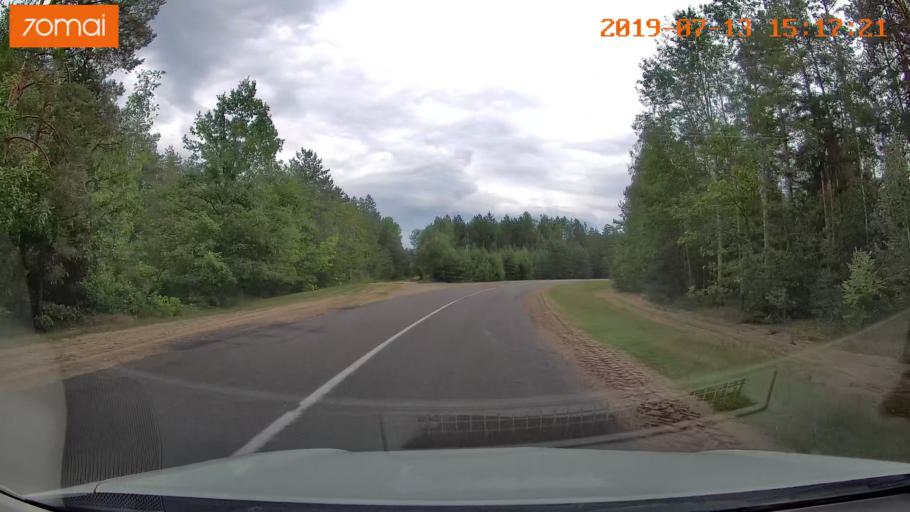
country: BY
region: Mogilev
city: Hlusha
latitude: 53.0969
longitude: 28.8437
